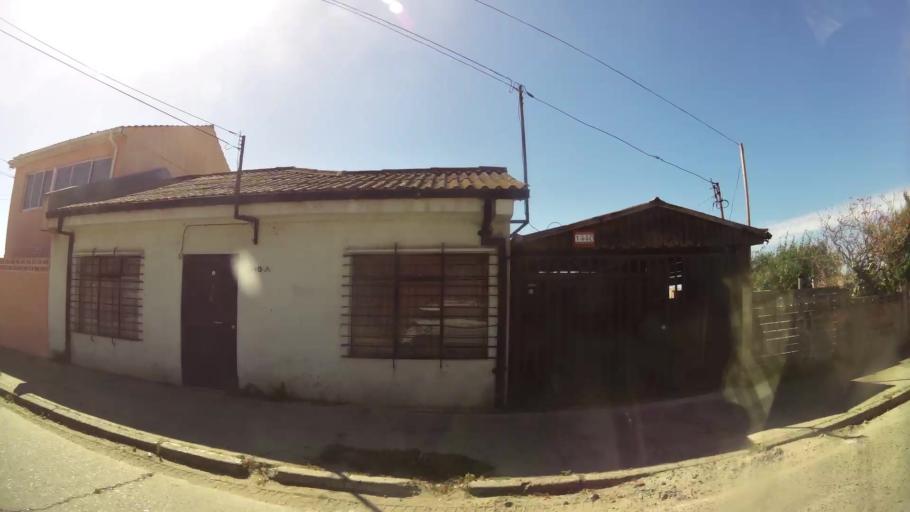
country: CL
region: Valparaiso
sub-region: Provincia de Valparaiso
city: Vina del Mar
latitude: -33.0326
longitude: -71.5753
